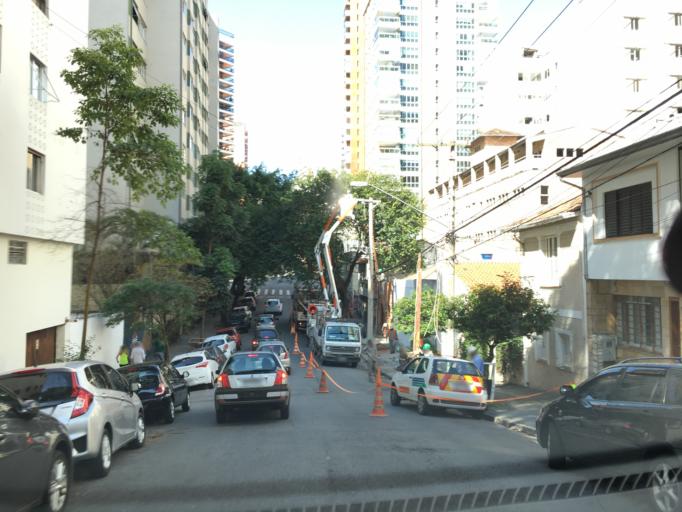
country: BR
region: Sao Paulo
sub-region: Sao Paulo
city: Sao Paulo
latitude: -23.5340
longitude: -46.6815
